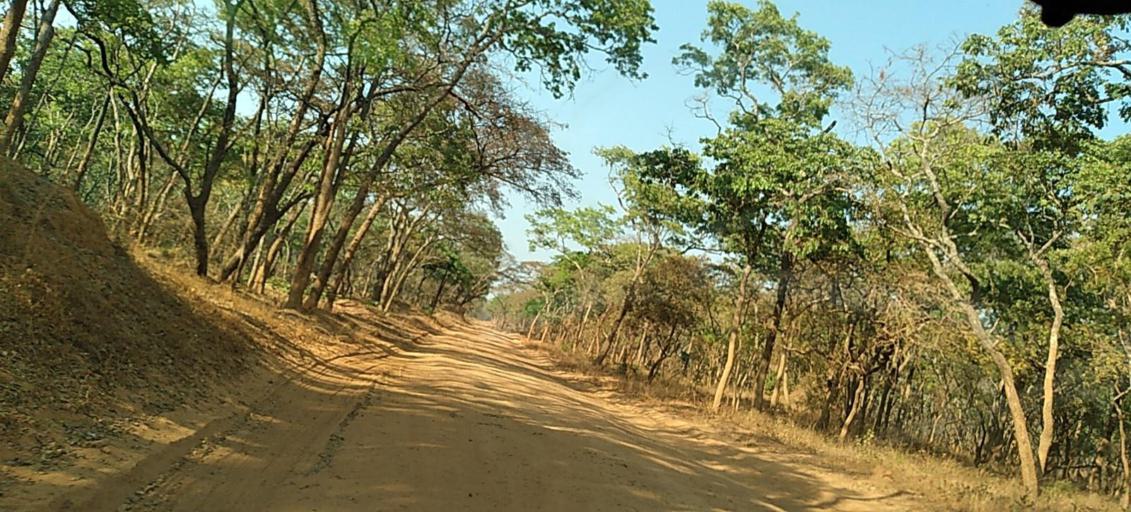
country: ZM
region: North-Western
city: Kasempa
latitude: -13.5868
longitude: 25.9861
